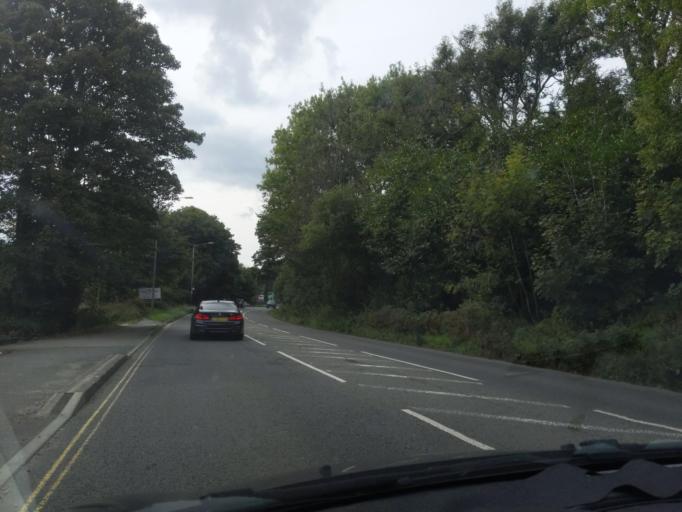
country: GB
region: England
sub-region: Cornwall
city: Par
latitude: 50.3472
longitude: -4.7367
